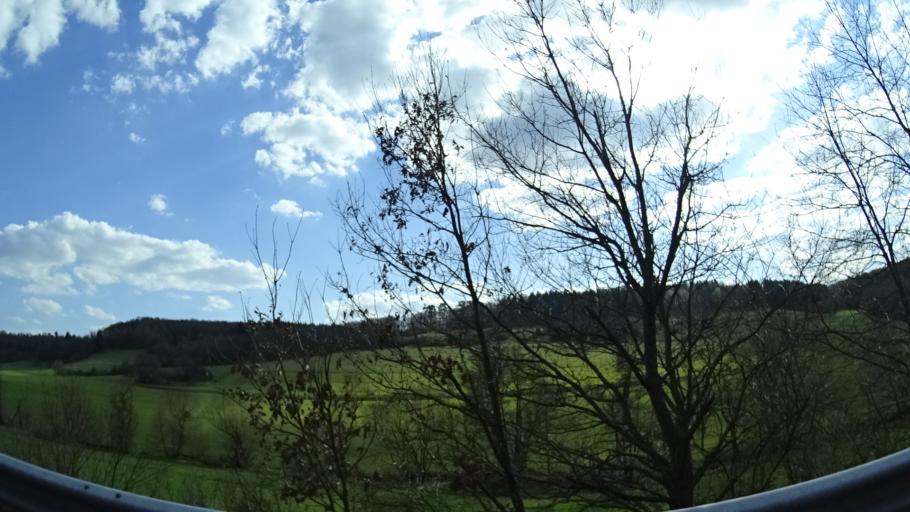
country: DE
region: Rheinland-Pfalz
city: Mittelreidenbach
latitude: 49.7406
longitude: 7.4510
